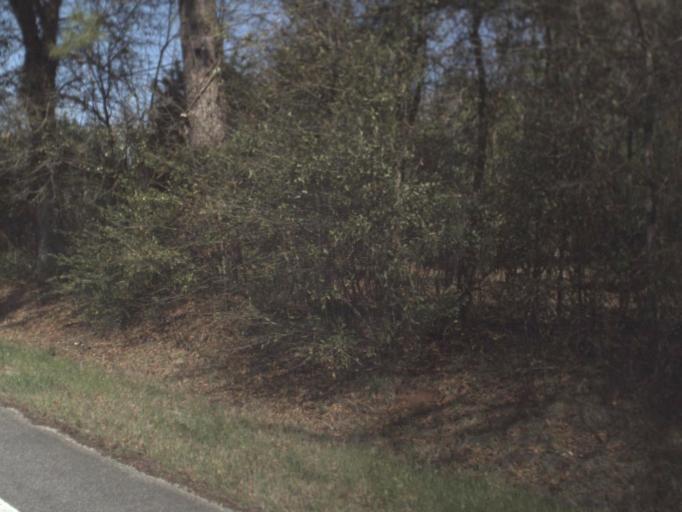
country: US
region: Florida
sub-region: Gadsden County
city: Gretna
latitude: 30.6527
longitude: -84.6026
